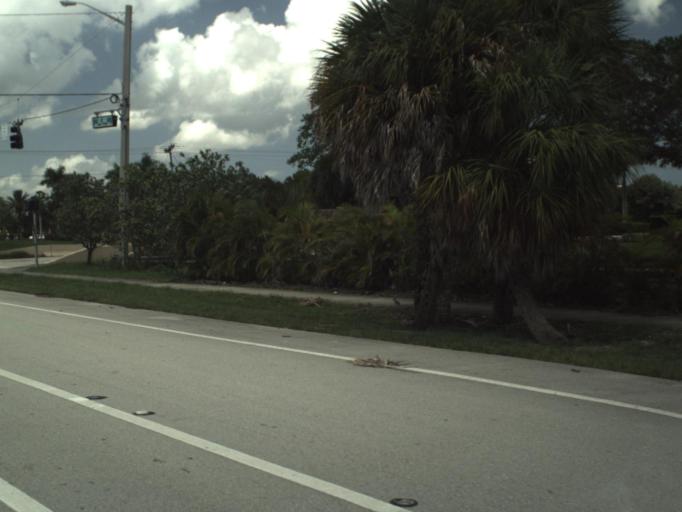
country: US
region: Florida
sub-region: Palm Beach County
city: Kings Point
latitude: 26.4059
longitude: -80.2038
